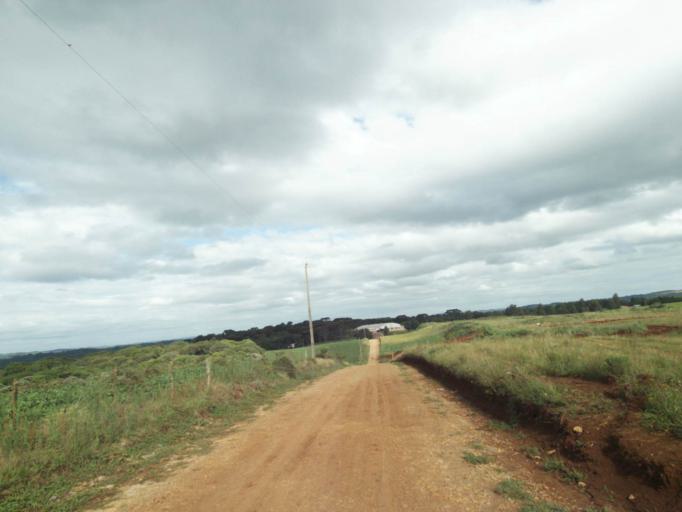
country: BR
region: Rio Grande do Sul
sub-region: Lagoa Vermelha
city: Lagoa Vermelha
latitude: -28.2028
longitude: -51.5130
